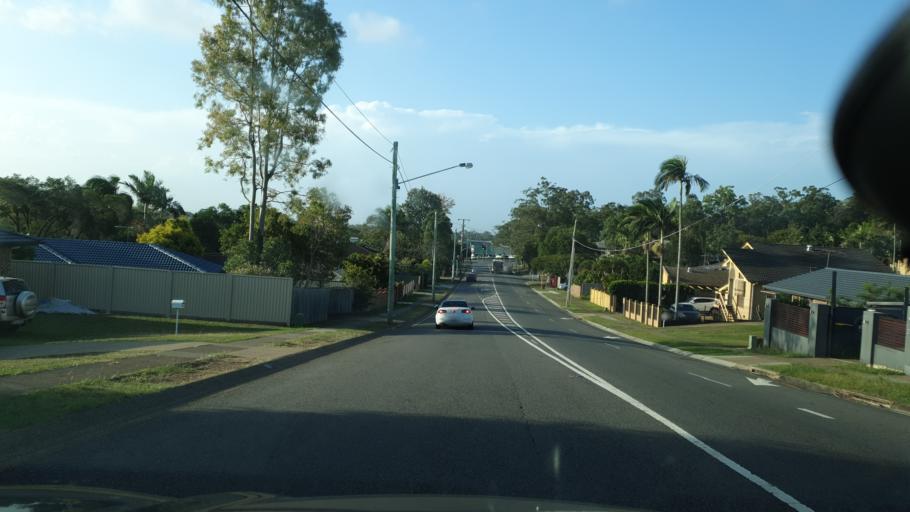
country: AU
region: Queensland
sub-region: Brisbane
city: Belmont
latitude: -27.4876
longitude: 153.1270
